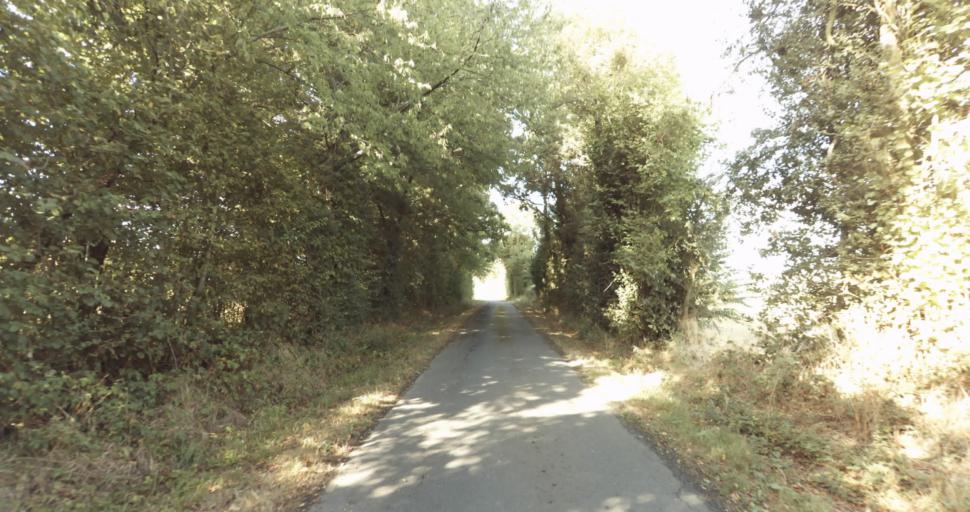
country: FR
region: Lower Normandy
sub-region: Departement de l'Orne
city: Vimoutiers
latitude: 48.9251
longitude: 0.1180
